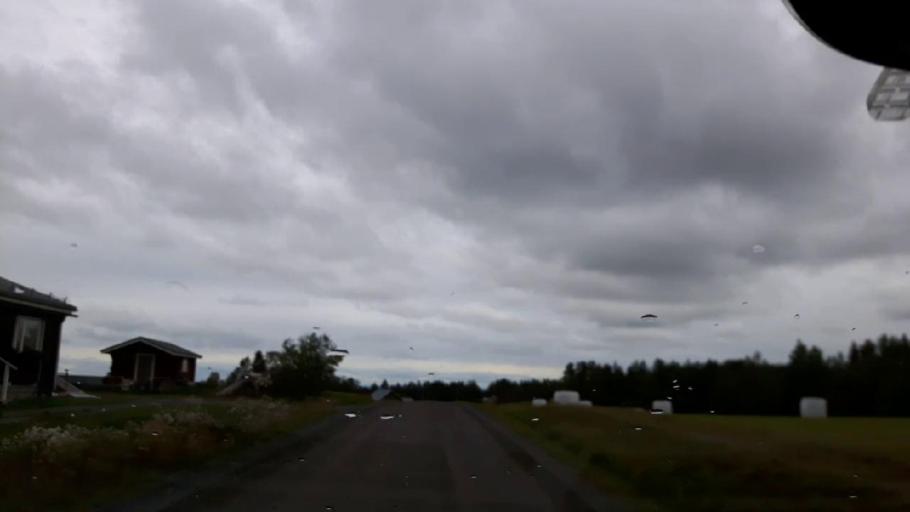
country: SE
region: Jaemtland
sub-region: OEstersunds Kommun
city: Ostersund
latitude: 63.0549
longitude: 14.5624
